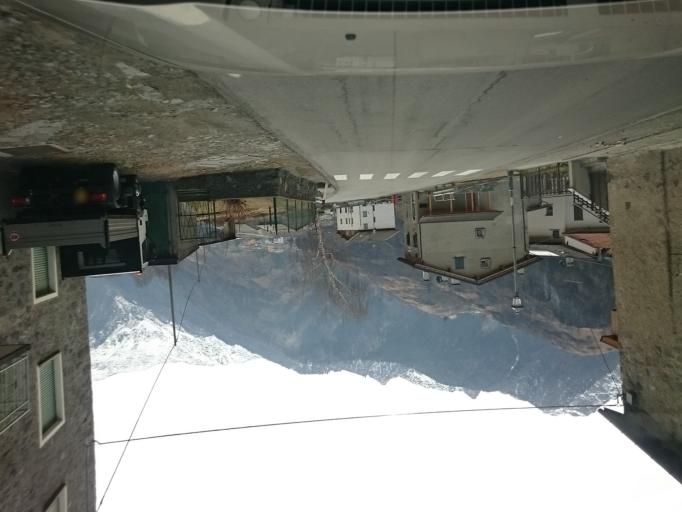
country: IT
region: Lombardy
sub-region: Provincia di Sondrio
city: Sondalo
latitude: 46.3553
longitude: 10.3559
